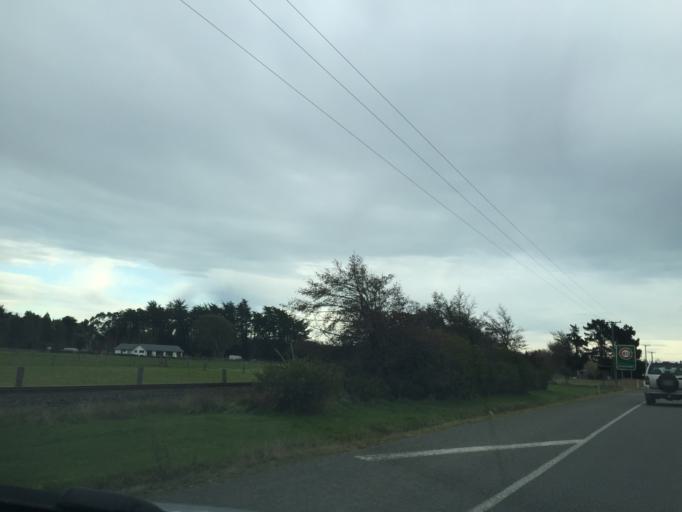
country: NZ
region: Southland
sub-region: Invercargill City
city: Invercargill
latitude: -46.4003
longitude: 168.4134
